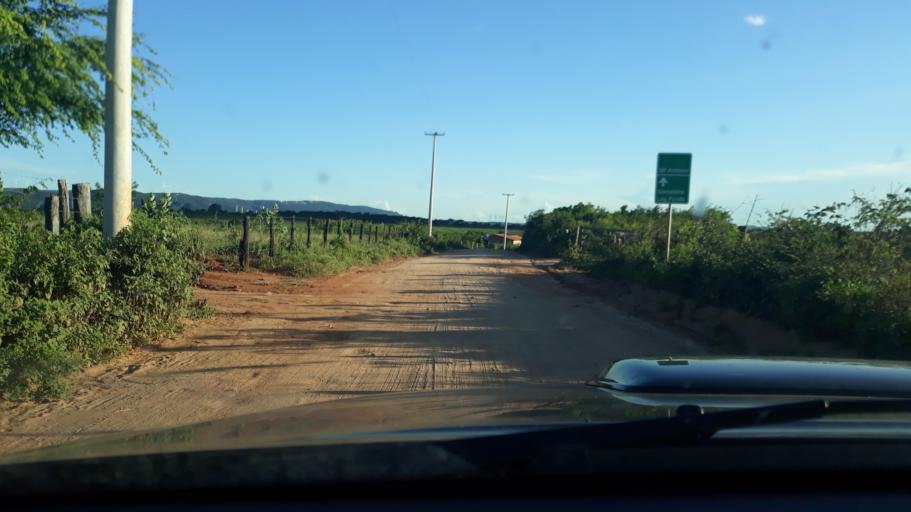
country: BR
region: Bahia
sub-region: Riacho De Santana
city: Riacho de Santana
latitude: -13.7940
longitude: -42.7118
